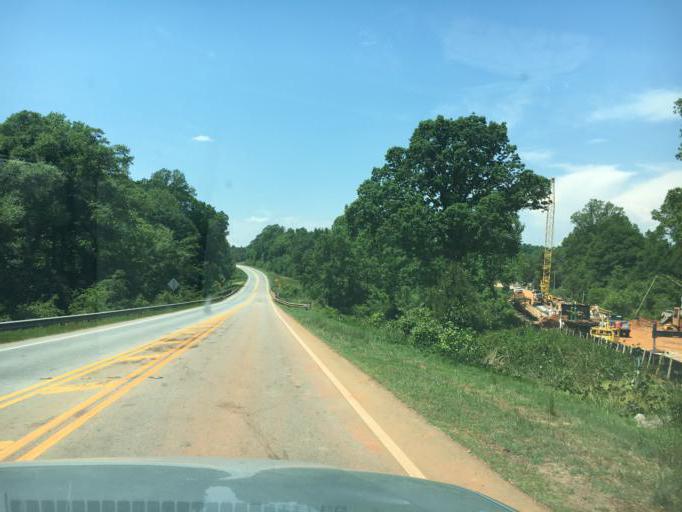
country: US
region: Georgia
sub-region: Hart County
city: Royston
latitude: 34.2886
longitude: -83.0612
